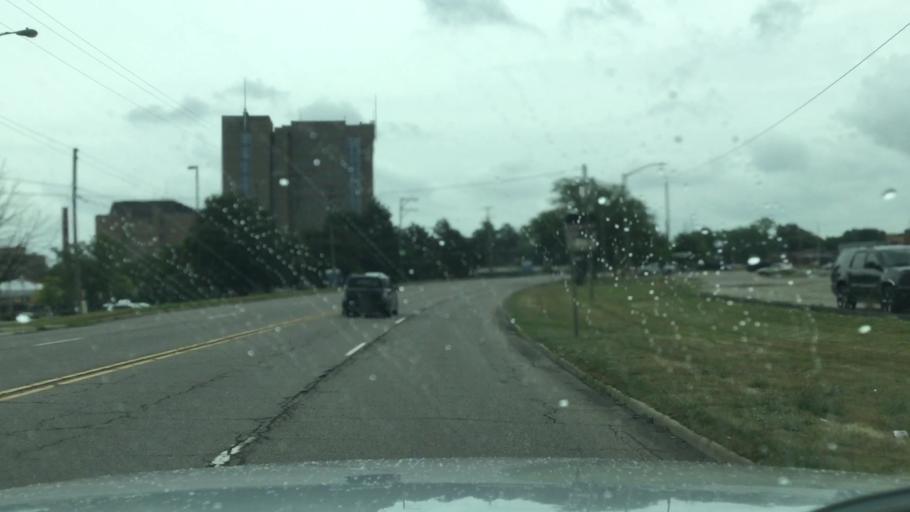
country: US
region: Michigan
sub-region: Genesee County
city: Flint
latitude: 43.0145
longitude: -83.7364
